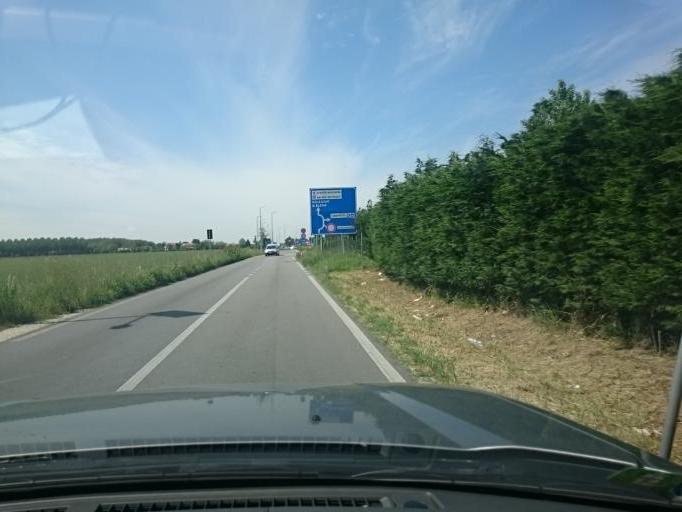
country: IT
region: Veneto
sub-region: Provincia di Padova
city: Sant'Elena
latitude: 45.2053
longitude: 11.7268
